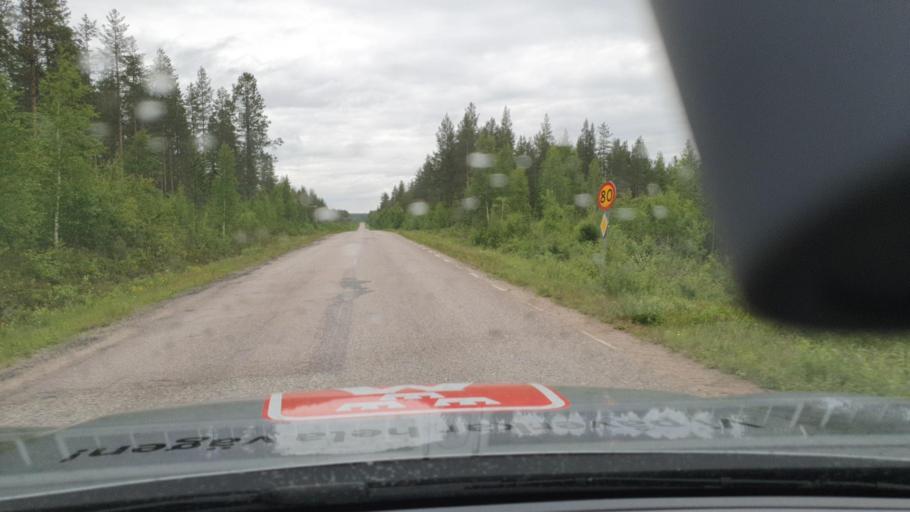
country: SE
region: Norrbotten
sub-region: Overkalix Kommun
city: OEverkalix
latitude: 66.3871
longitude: 22.7924
